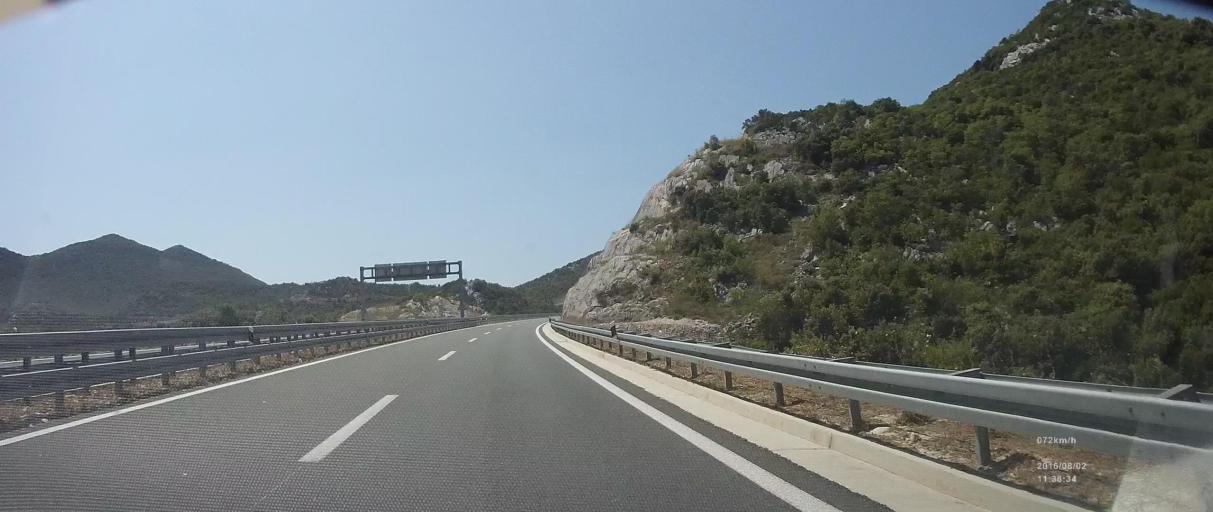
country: HR
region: Dubrovacko-Neretvanska
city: Komin
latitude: 43.0946
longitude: 17.4909
